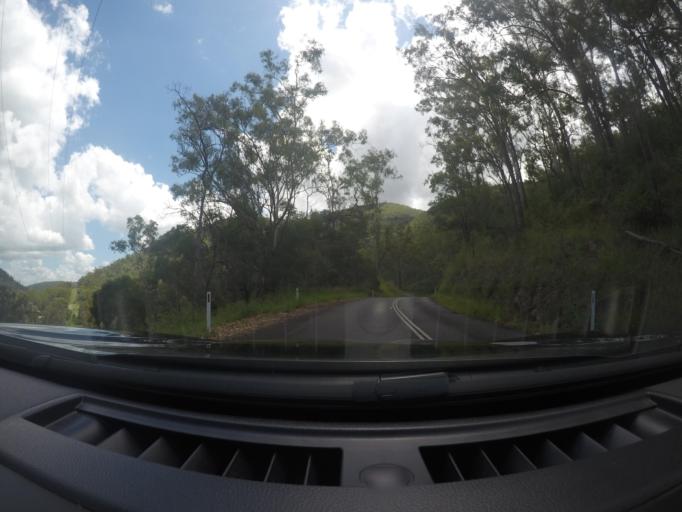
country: AU
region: Queensland
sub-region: Moreton Bay
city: Woodford
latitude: -27.1004
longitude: 152.5622
